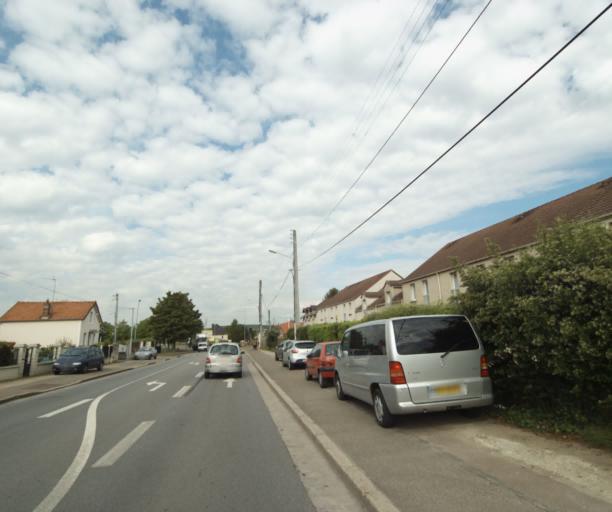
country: FR
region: Ile-de-France
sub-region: Departement des Yvelines
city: Les Mureaux
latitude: 48.9991
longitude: 1.9182
